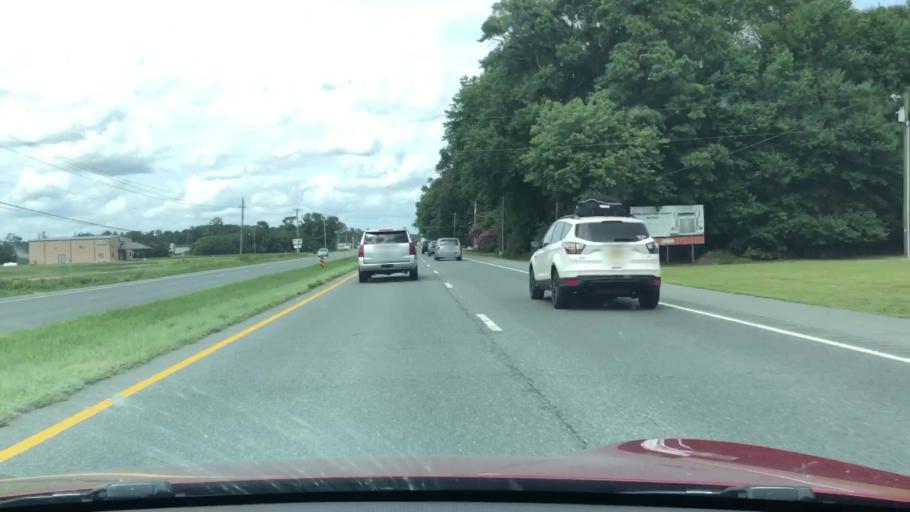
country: US
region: Virginia
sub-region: Accomack County
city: Wattsville
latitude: 37.9019
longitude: -75.5487
